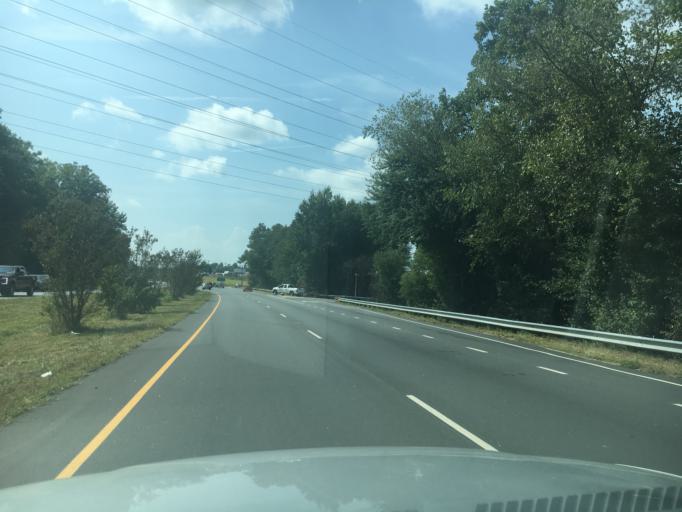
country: US
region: North Carolina
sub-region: Rutherford County
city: Forest City
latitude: 35.3376
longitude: -81.8959
